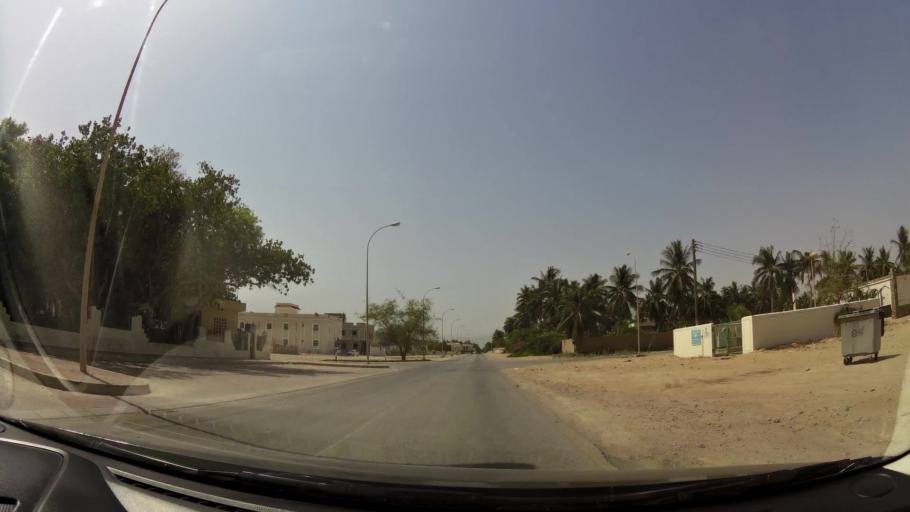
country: OM
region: Zufar
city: Salalah
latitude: 17.0143
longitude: 54.0730
